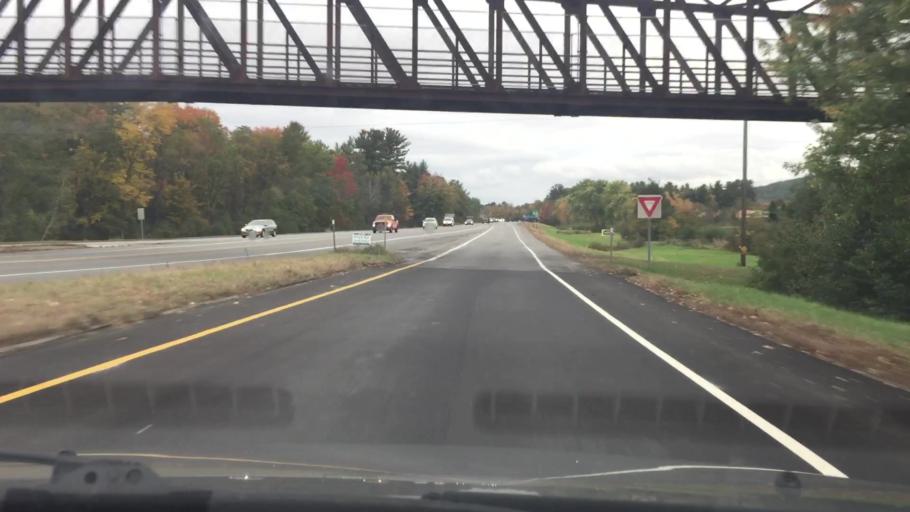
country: US
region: New Hampshire
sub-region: Cheshire County
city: Keene
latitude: 42.9316
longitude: -72.2981
